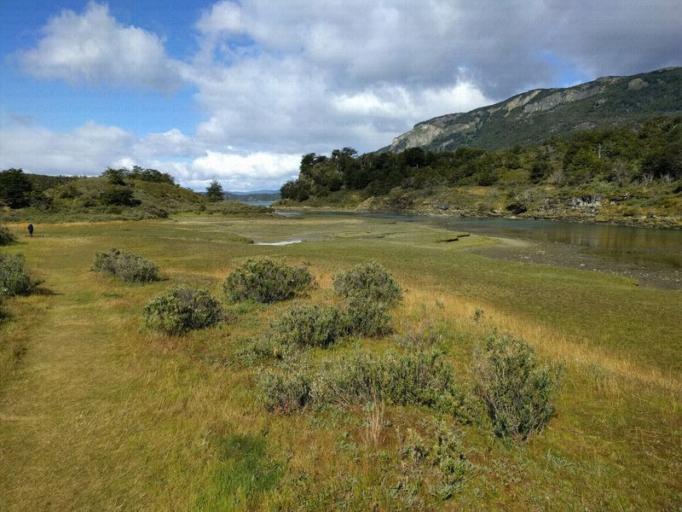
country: AR
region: Tierra del Fuego
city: Ushuaia
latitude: -54.8481
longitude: -68.5768
